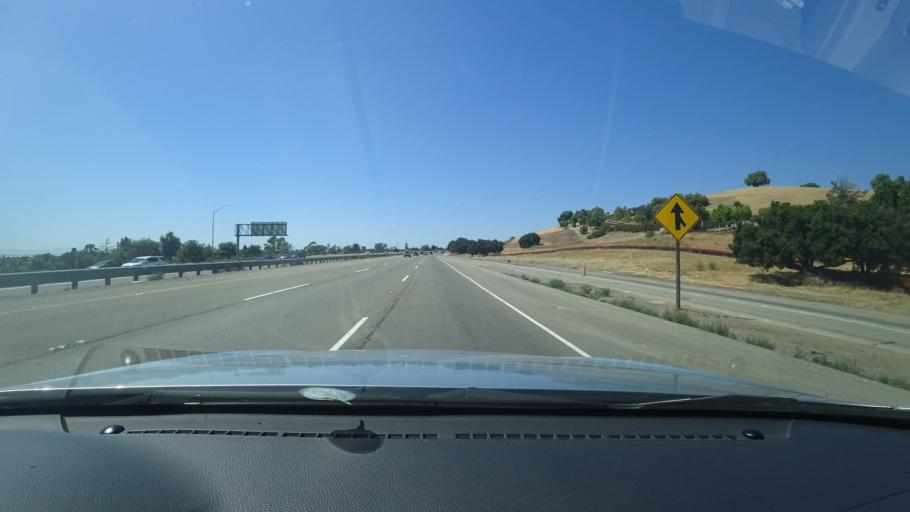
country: US
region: California
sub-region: Santa Clara County
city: Milpitas
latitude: 37.4690
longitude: -121.9075
